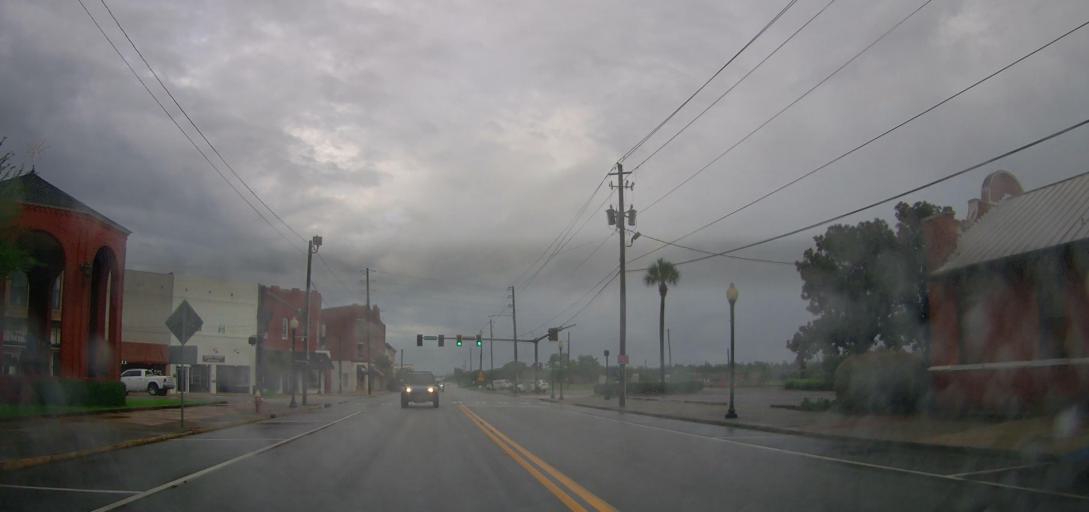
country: US
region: Georgia
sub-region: Ware County
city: Waycross
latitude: 31.2100
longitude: -82.3586
